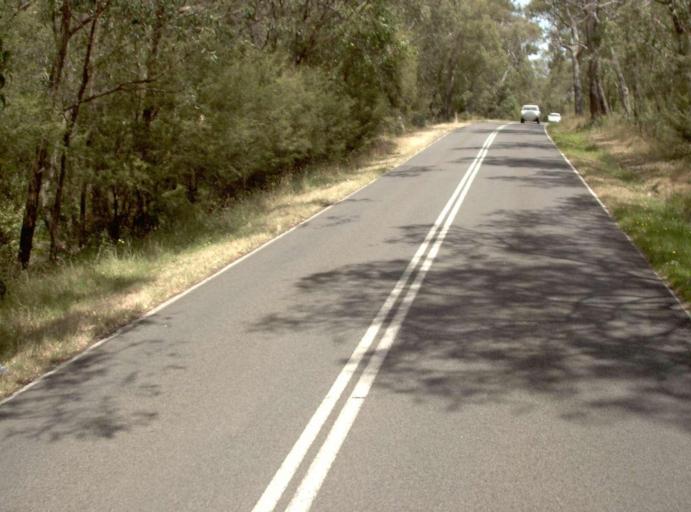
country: AU
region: Victoria
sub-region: Latrobe
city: Moe
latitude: -38.1022
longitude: 146.2987
